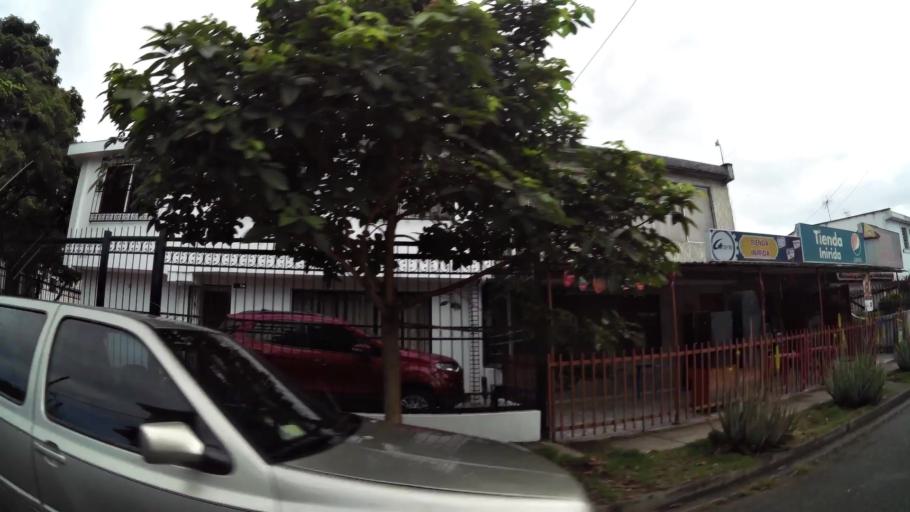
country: CO
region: Valle del Cauca
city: Cali
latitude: 3.4824
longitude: -76.5177
